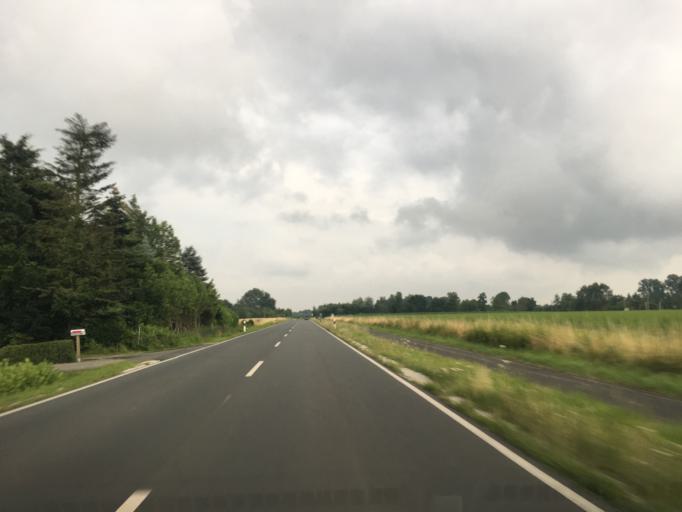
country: DE
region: North Rhine-Westphalia
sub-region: Regierungsbezirk Munster
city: Greven
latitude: 52.0501
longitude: 7.6161
